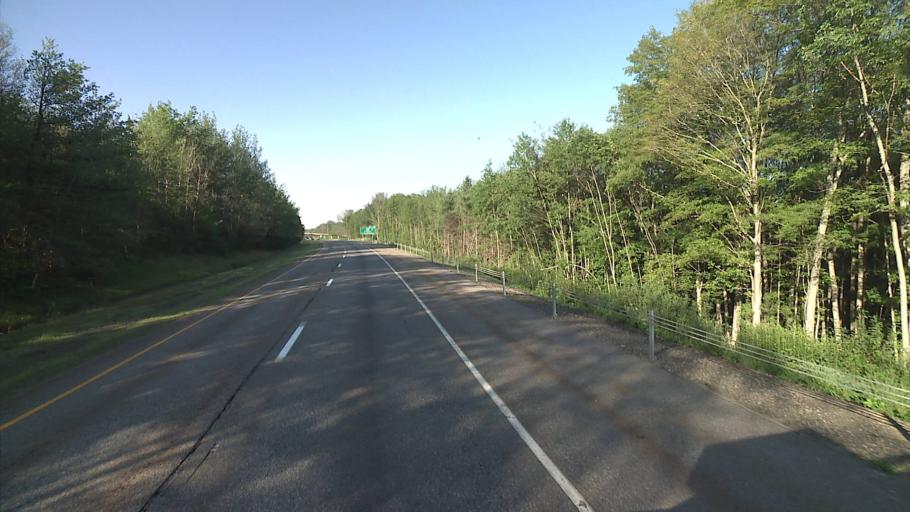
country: US
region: Connecticut
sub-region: Windham County
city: Thompson
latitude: 41.9707
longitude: -71.8698
